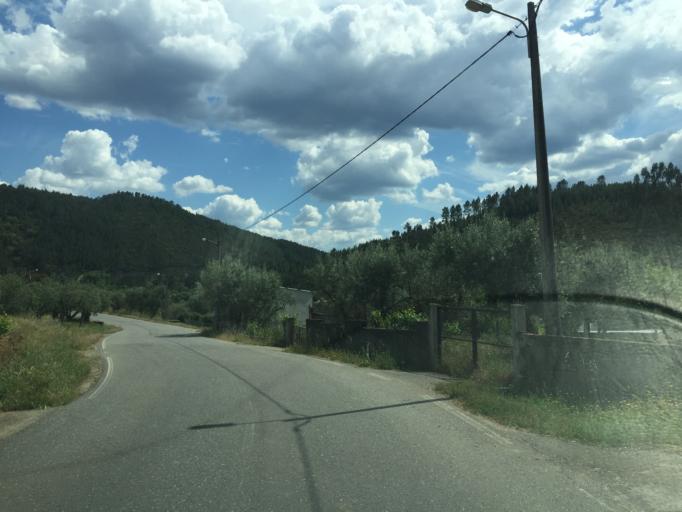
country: PT
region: Coimbra
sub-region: Pampilhosa da Serra
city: Pampilhosa da Serra
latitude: 40.0646
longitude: -7.8010
